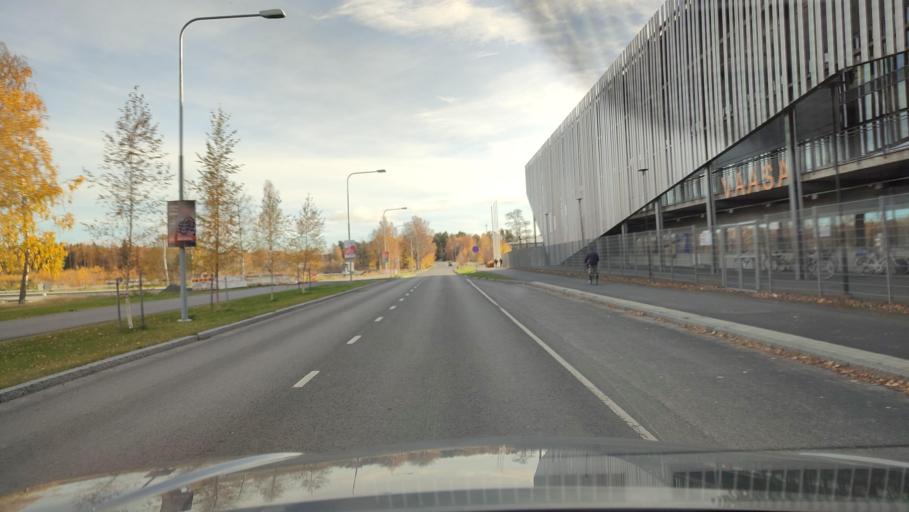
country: FI
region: Ostrobothnia
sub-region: Vaasa
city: Vaasa
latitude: 63.0858
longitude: 21.6286
